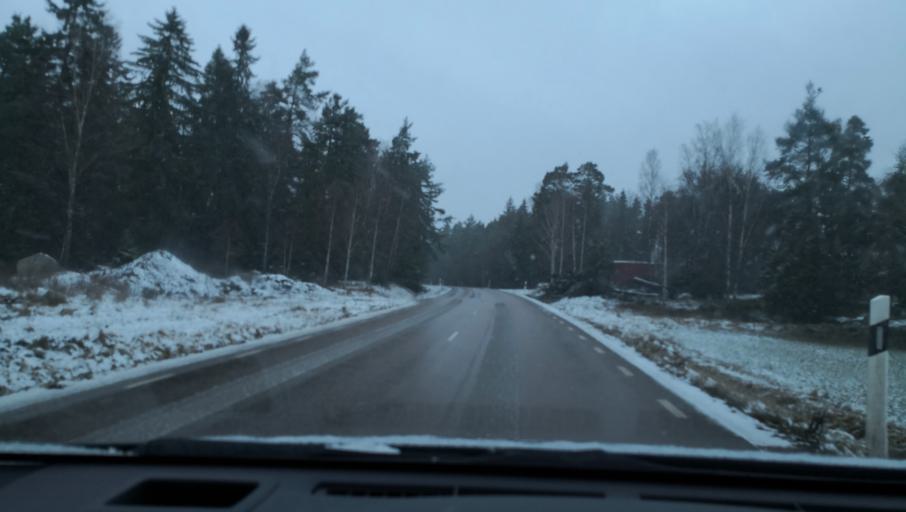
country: SE
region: Vaestmanland
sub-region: Hallstahammars Kommun
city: Kolback
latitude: 59.5869
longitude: 16.3561
